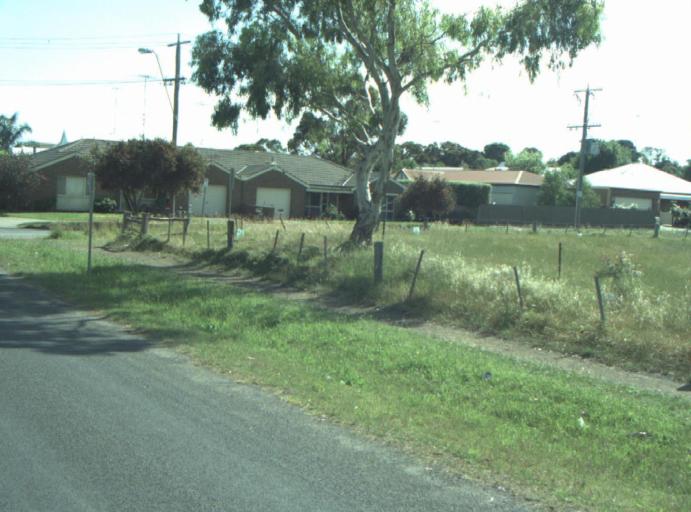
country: AU
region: Victoria
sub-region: Greater Geelong
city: Clifton Springs
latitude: -38.1654
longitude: 144.5538
